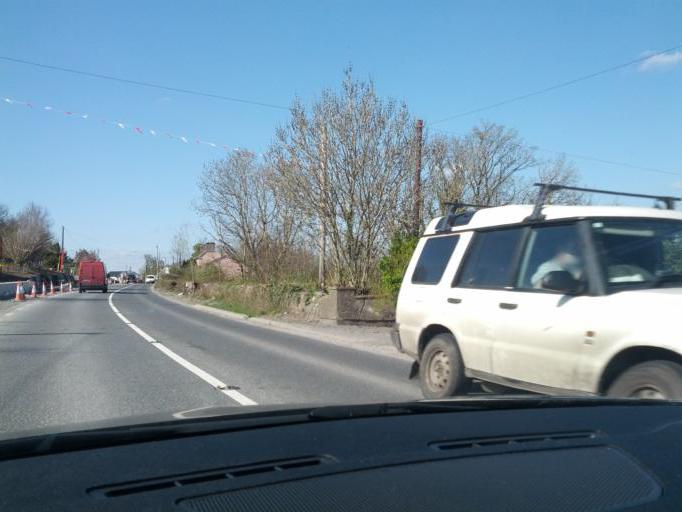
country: IE
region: Connaught
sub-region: County Galway
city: Moycullen
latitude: 53.3309
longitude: -9.1712
